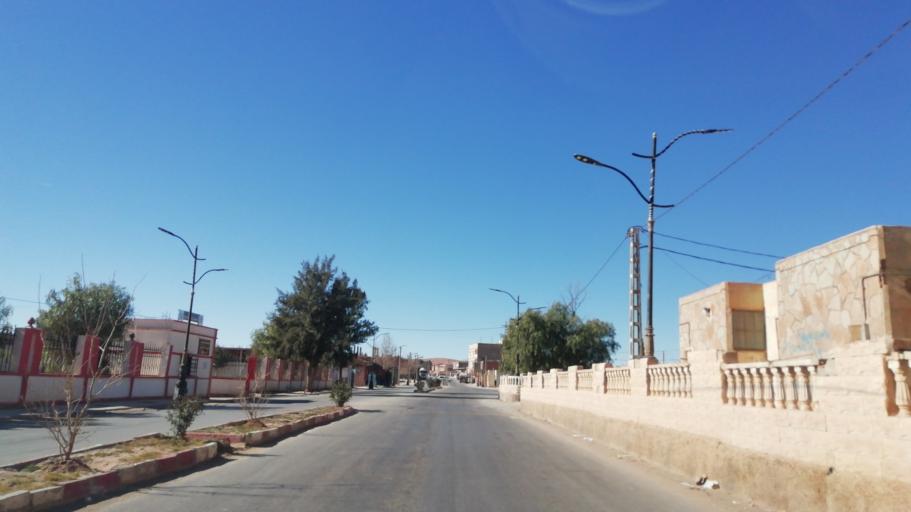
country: DZ
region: El Bayadh
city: El Bayadh
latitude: 33.7284
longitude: 1.5401
